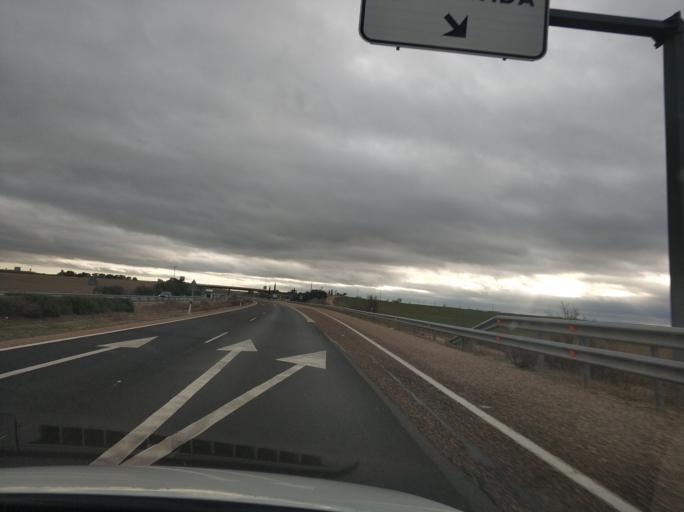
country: ES
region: Castille and Leon
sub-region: Provincia de Salamanca
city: Pajares de la Laguna
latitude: 41.0967
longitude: -5.5014
